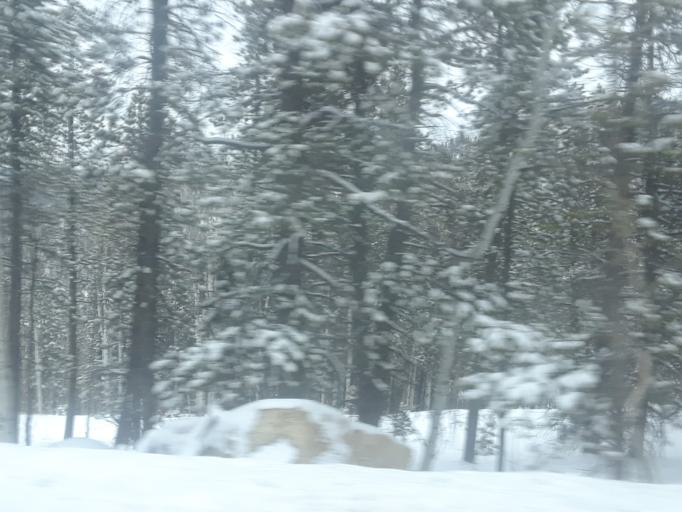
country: US
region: Colorado
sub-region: Boulder County
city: Coal Creek
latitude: 39.9254
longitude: -105.4175
